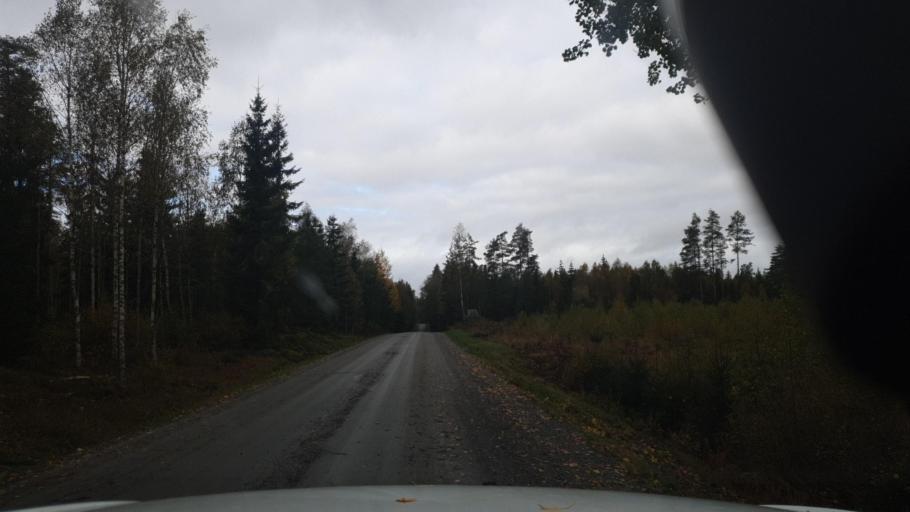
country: SE
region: Vaermland
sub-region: Karlstads Kommun
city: Valberg
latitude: 59.4492
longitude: 13.1084
